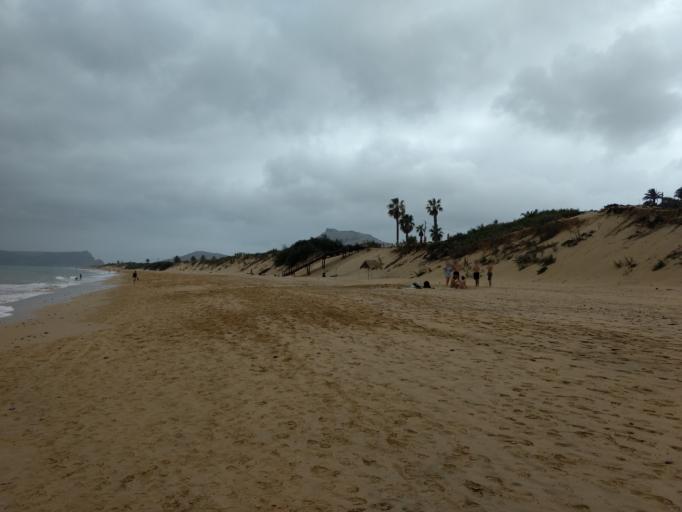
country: PT
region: Madeira
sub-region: Porto Santo
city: Vila de Porto Santo
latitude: 33.0541
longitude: -16.3401
